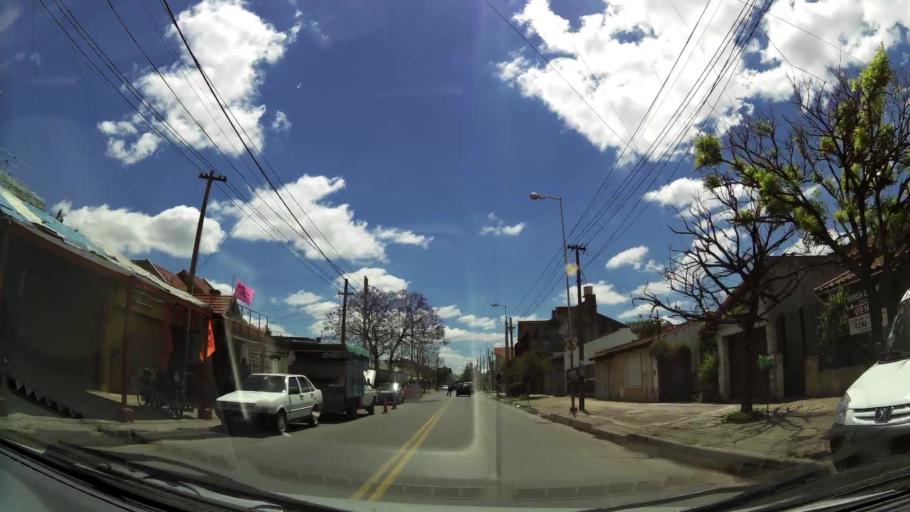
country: AR
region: Buenos Aires
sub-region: Partido de Lomas de Zamora
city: Lomas de Zamora
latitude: -34.7304
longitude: -58.4152
